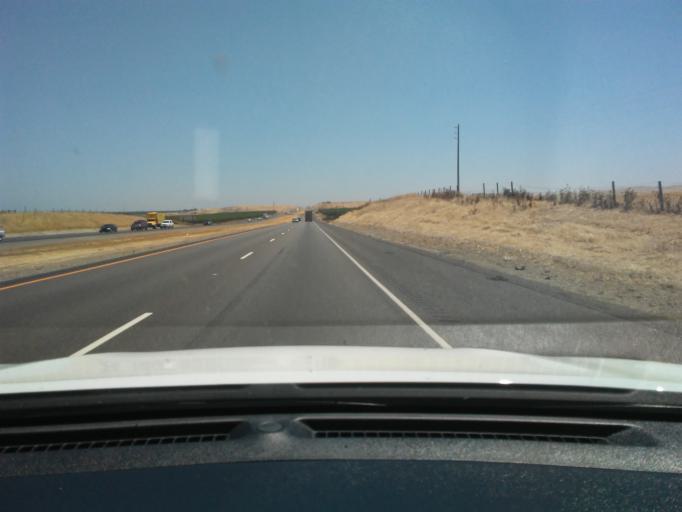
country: US
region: California
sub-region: Stanislaus County
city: Patterson
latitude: 37.4098
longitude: -121.1472
